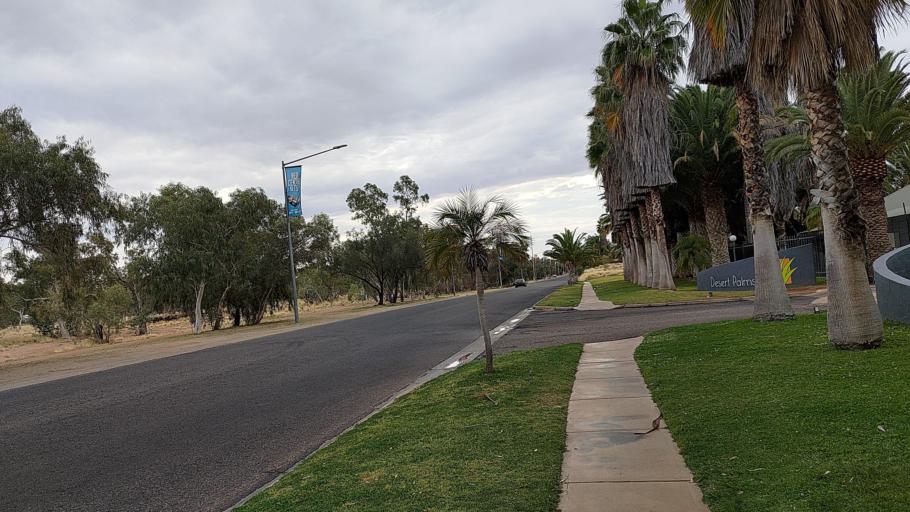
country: AU
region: Northern Territory
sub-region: Alice Springs
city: Alice Springs
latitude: -23.7137
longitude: 133.8794
